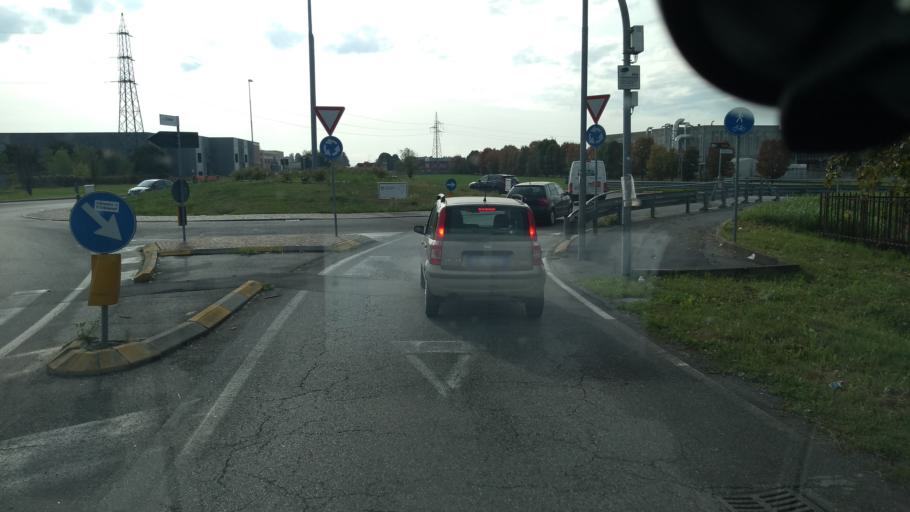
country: IT
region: Lombardy
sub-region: Provincia di Bergamo
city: Urgnano
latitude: 45.6195
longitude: 9.6916
